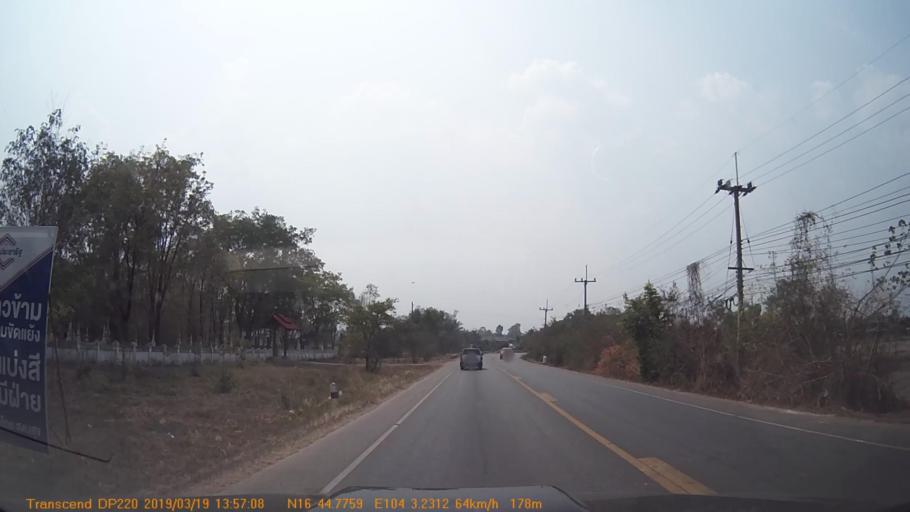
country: TH
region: Kalasin
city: Na Khu
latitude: 16.7463
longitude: 104.0534
